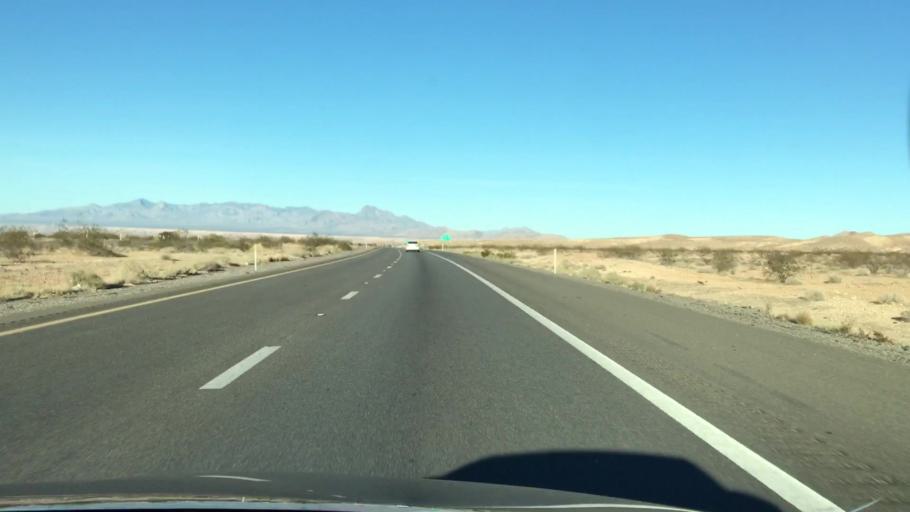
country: US
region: Nevada
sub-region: Clark County
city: Moapa Town
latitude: 36.5844
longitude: -114.6520
